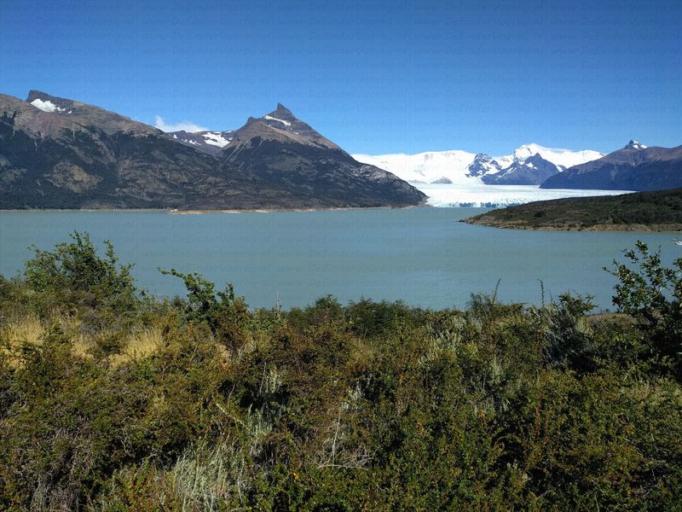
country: AR
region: Santa Cruz
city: El Calafate
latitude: -50.4754
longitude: -72.9811
